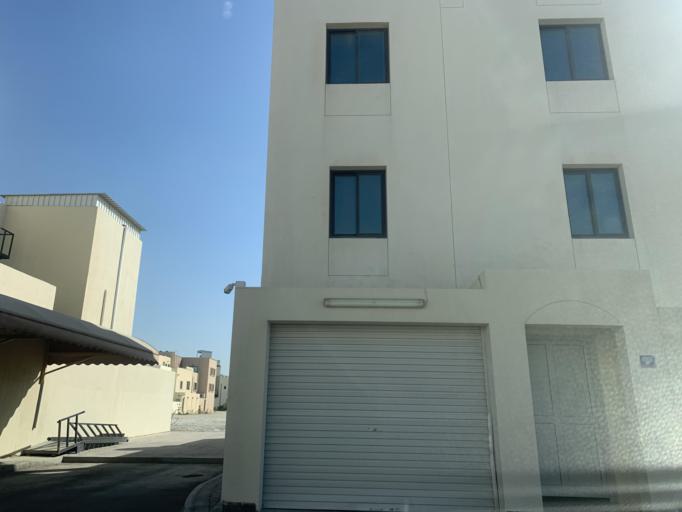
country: BH
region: Central Governorate
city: Madinat Hamad
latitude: 26.1253
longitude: 50.4822
